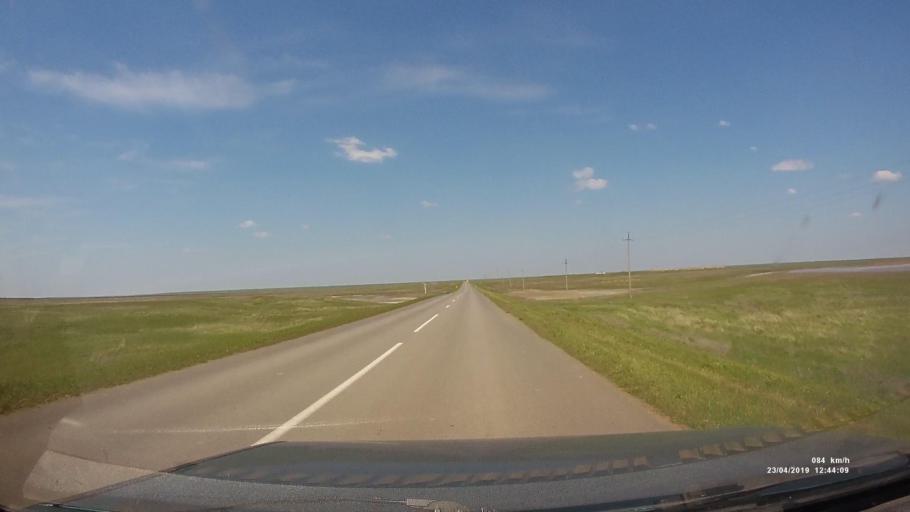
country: RU
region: Kalmykiya
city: Yashalta
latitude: 46.4731
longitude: 42.6489
